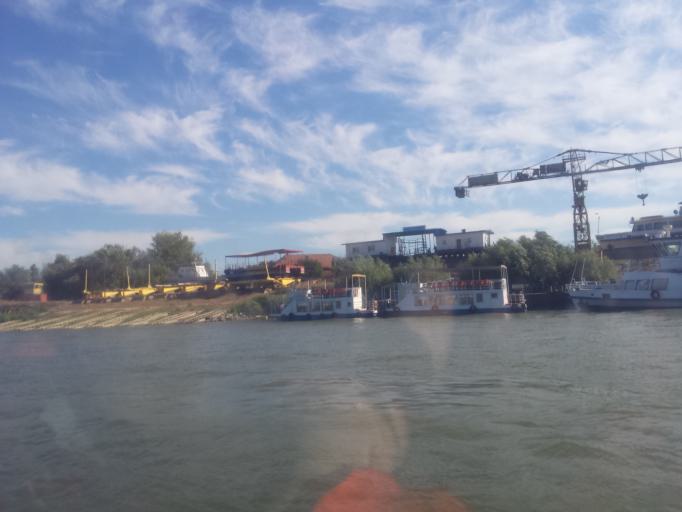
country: RO
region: Tulcea
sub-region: Municipiul Tulcea
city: Tulcea
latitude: 45.1839
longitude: 28.8067
